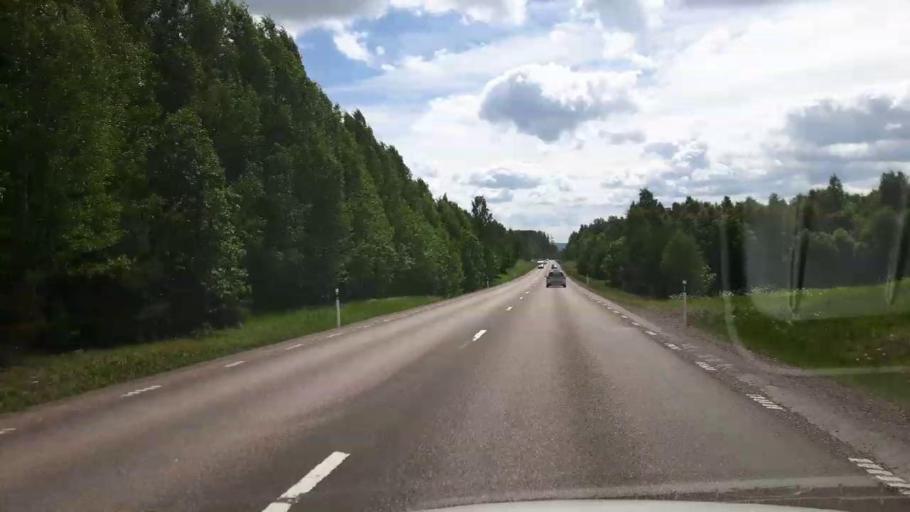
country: SE
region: Dalarna
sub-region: Saters Kommun
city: Saeter
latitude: 60.4618
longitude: 15.8009
